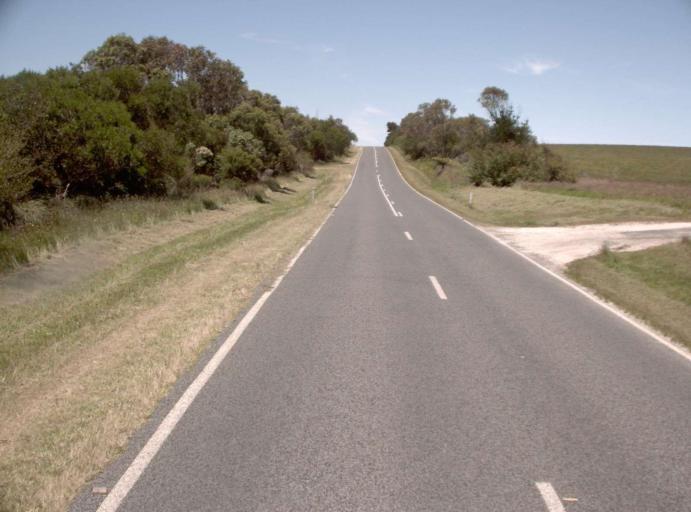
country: AU
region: Victoria
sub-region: Bass Coast
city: North Wonthaggi
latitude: -38.7628
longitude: 146.1519
